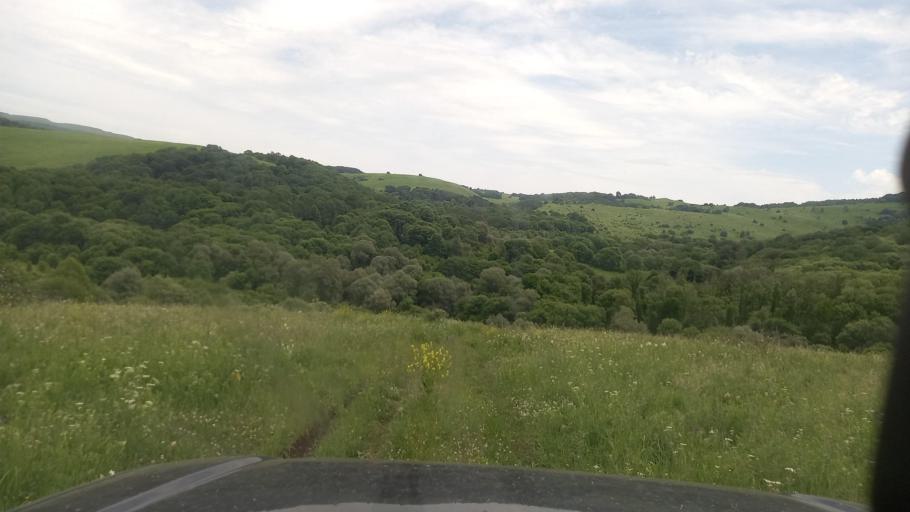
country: RU
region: Karachayevo-Cherkesiya
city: Pregradnaya
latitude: 44.0878
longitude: 41.1956
